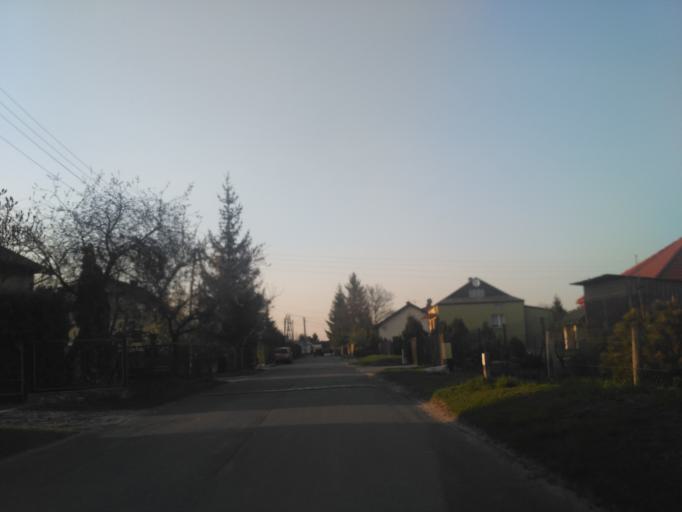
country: PL
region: Lublin Voivodeship
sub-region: Powiat chelmski
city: Pokrowka
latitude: 51.1116
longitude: 23.4835
